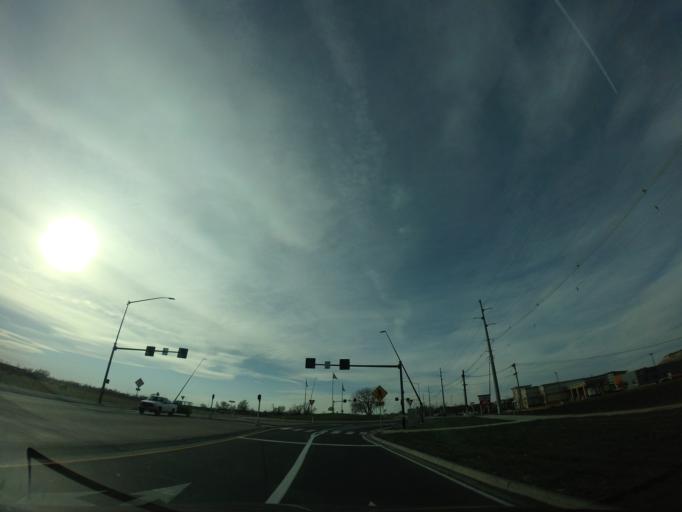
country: US
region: Montana
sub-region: Yellowstone County
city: Billings
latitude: 45.7842
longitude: -108.6104
